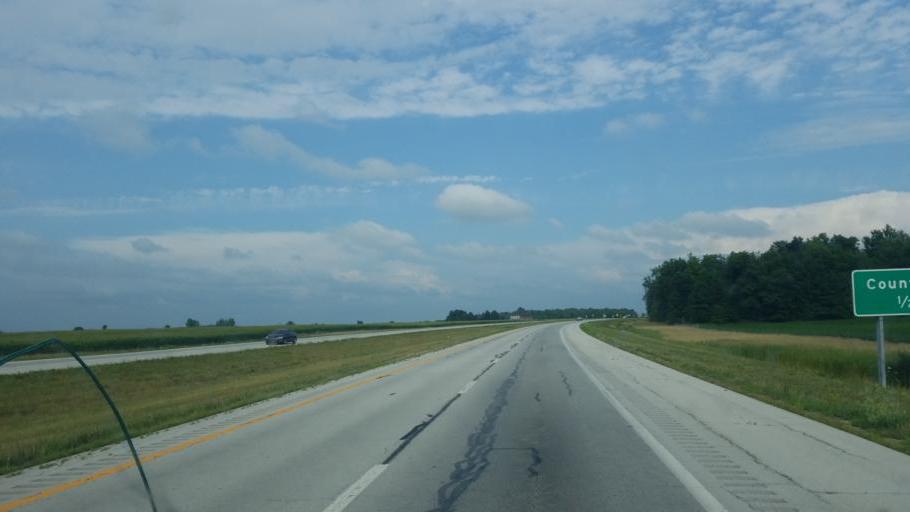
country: US
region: Ohio
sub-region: Hardin County
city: Forest
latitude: 40.8264
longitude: -83.4870
